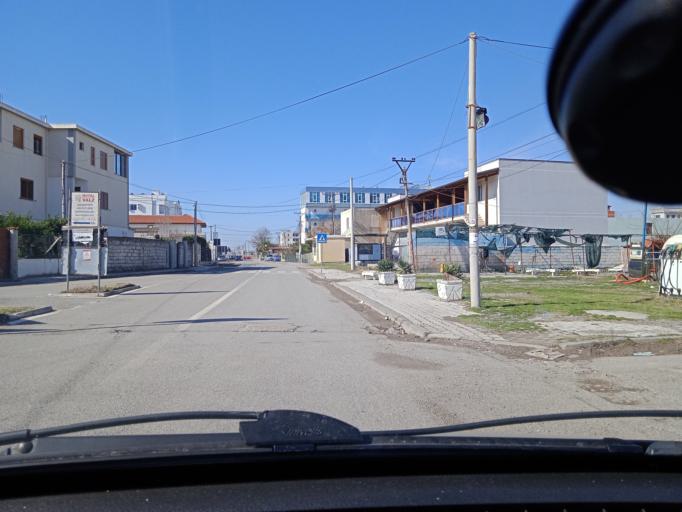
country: AL
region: Shkoder
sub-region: Rrethi i Shkodres
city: Velipoje
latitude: 41.8662
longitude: 19.4262
